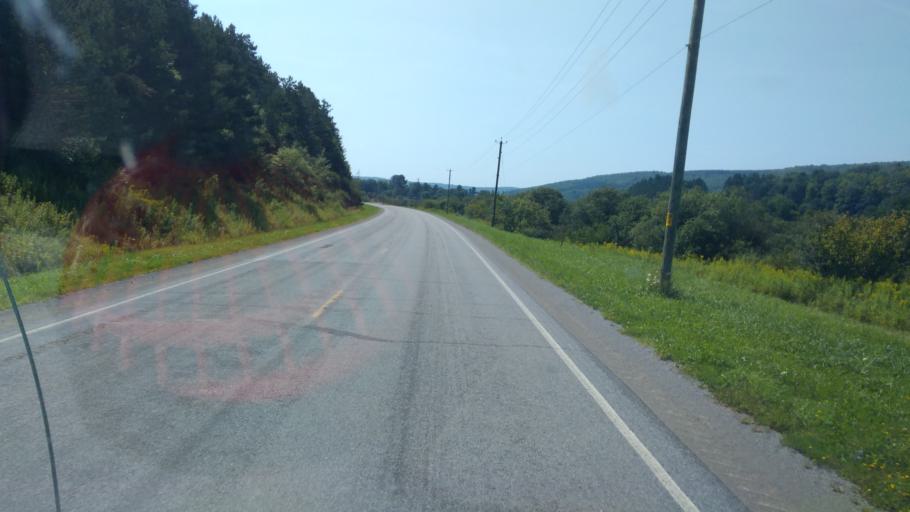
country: US
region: New York
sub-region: Allegany County
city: Belmont
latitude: 42.3270
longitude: -77.9368
